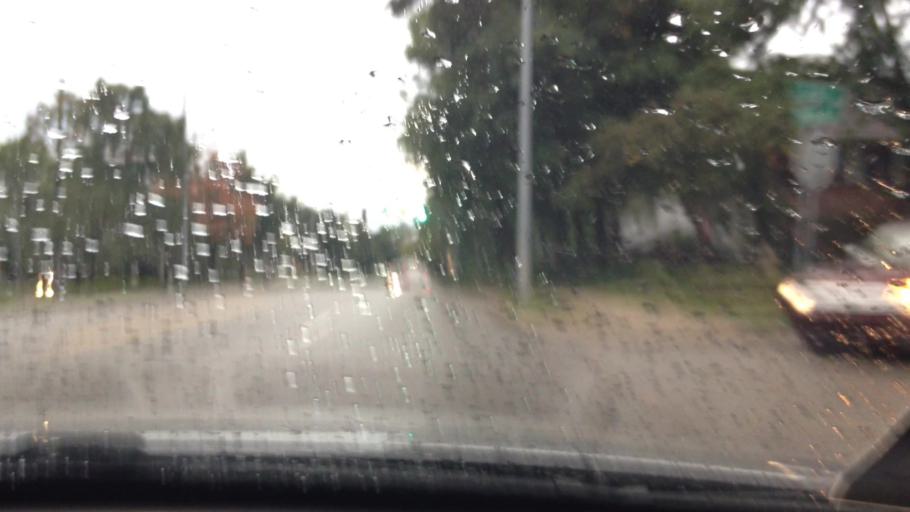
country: US
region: Kansas
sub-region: Johnson County
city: Mission Hills
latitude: 39.0059
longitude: -94.5934
